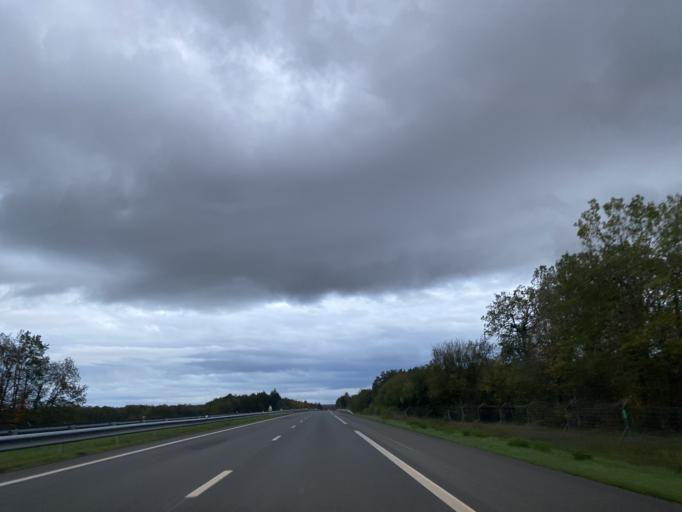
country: FR
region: Centre
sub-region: Departement du Cher
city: Levet
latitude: 46.8782
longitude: 2.4222
